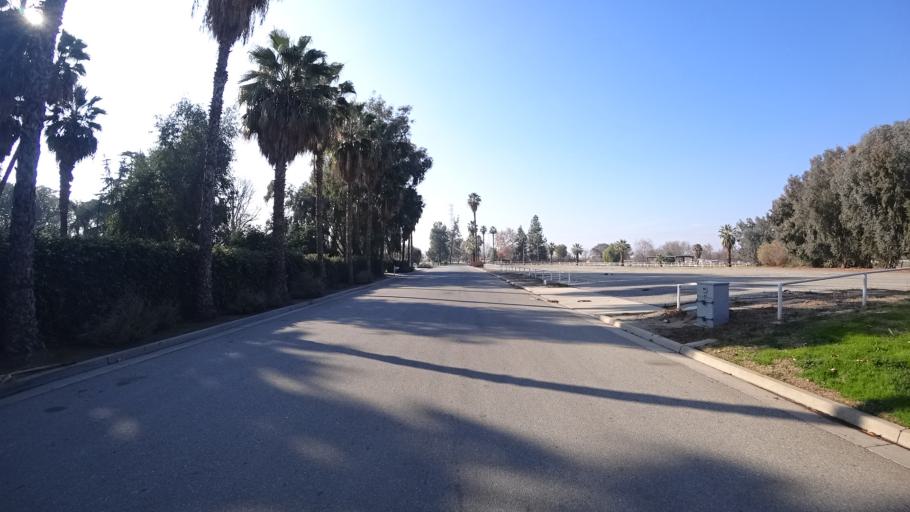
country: US
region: California
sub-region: Kern County
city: Oildale
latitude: 35.4048
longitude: -119.0034
